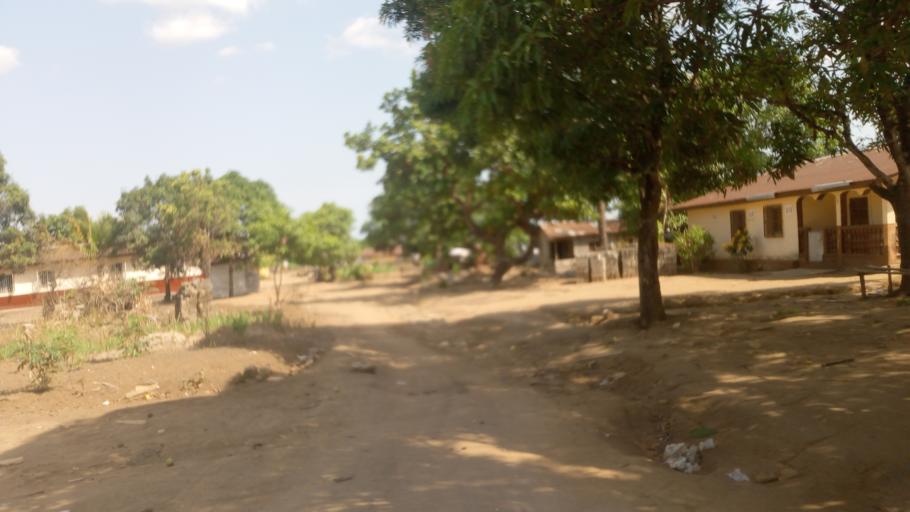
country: SL
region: Western Area
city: Waterloo
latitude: 8.3183
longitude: -13.0758
